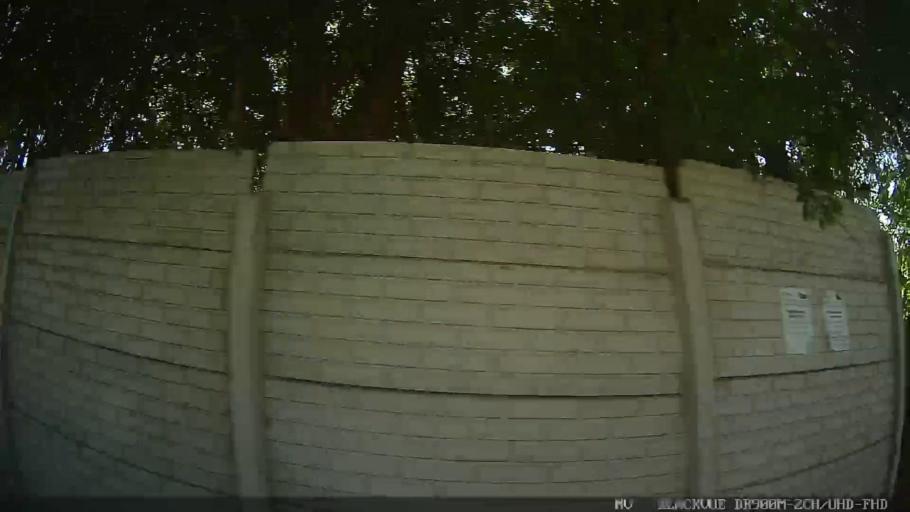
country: BR
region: Sao Paulo
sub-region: Atibaia
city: Atibaia
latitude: -23.1117
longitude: -46.5933
